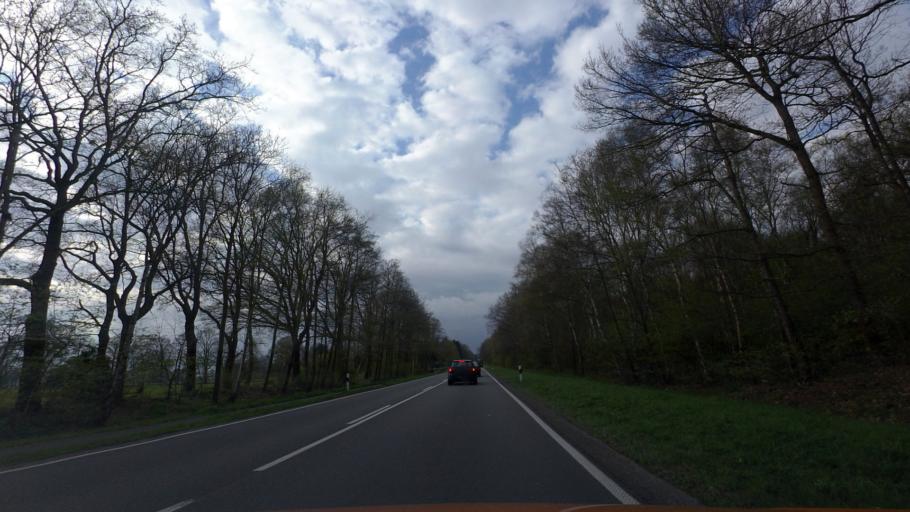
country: DE
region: Lower Saxony
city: Friesoythe
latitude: 52.9979
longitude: 7.8753
